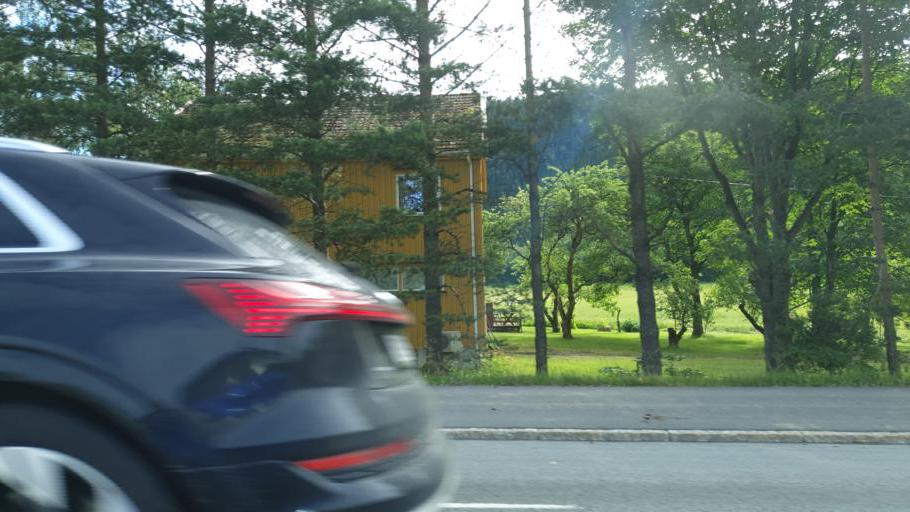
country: NO
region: Sor-Trondelag
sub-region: Melhus
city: Lundamo
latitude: 63.1697
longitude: 10.3143
